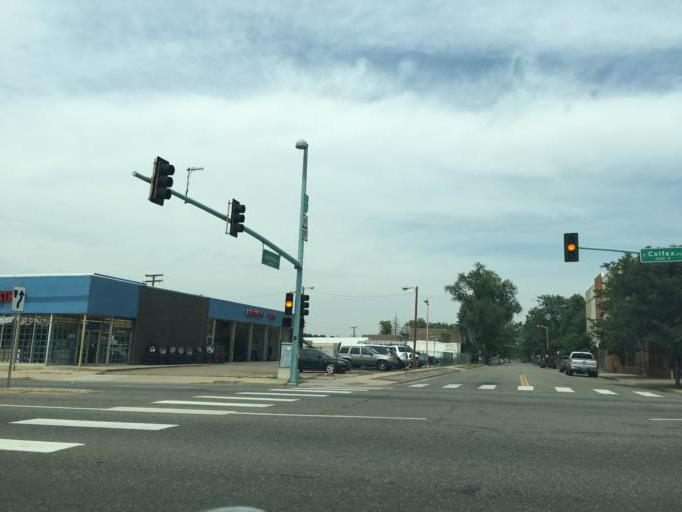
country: US
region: Colorado
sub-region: Adams County
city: Aurora
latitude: 39.7400
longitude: -104.8693
